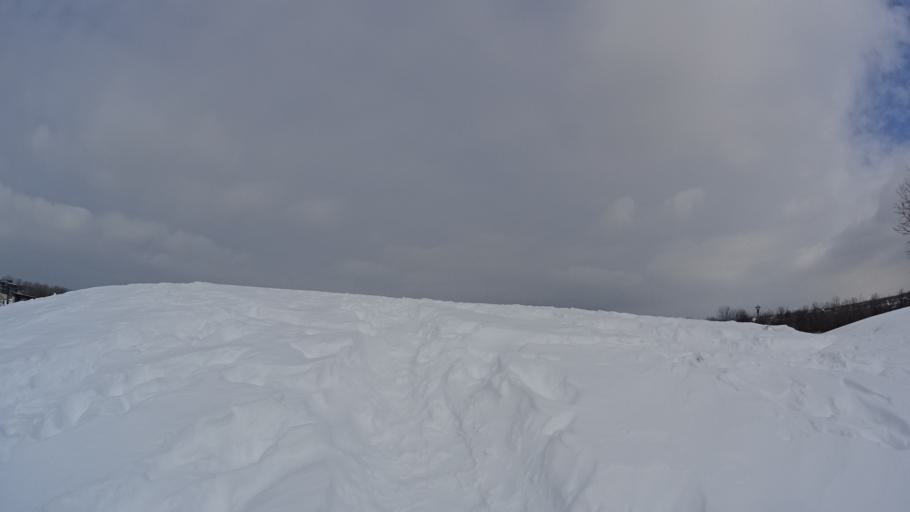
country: CA
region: Quebec
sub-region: Monteregie
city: Brossard
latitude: 45.4854
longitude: -73.4077
